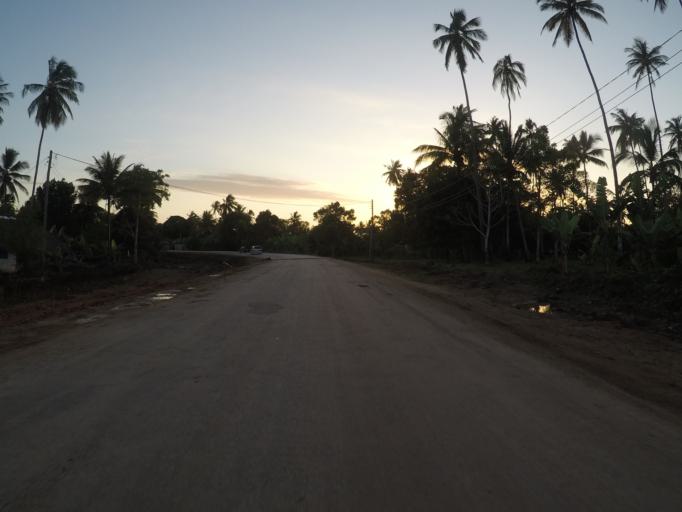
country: TZ
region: Zanzibar North
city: Gamba
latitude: -5.9805
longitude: 39.2892
